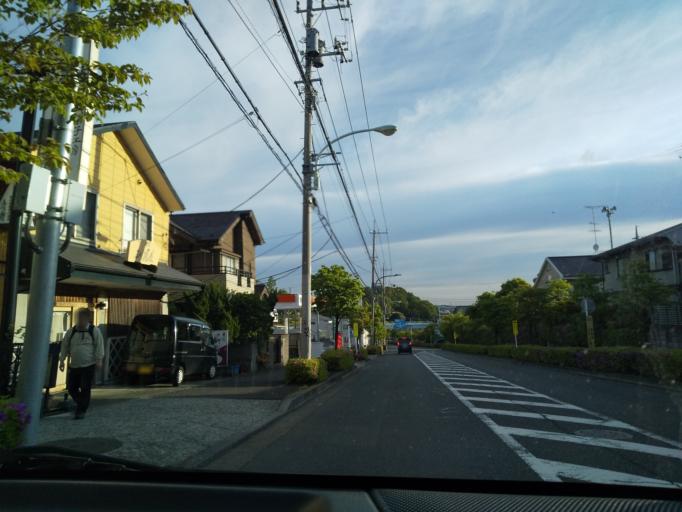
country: JP
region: Tokyo
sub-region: Machida-shi
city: Machida
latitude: 35.5687
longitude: 139.4540
